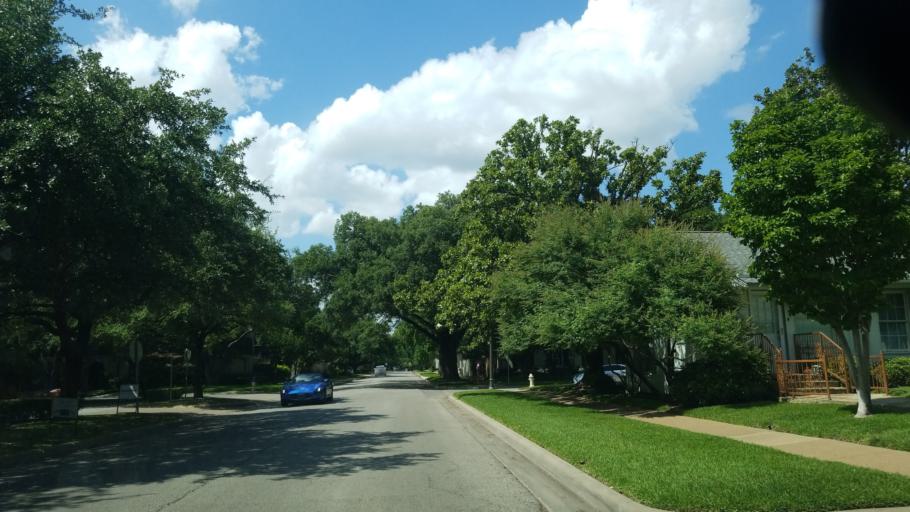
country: US
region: Texas
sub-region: Dallas County
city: Highland Park
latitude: 32.8300
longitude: -96.8191
